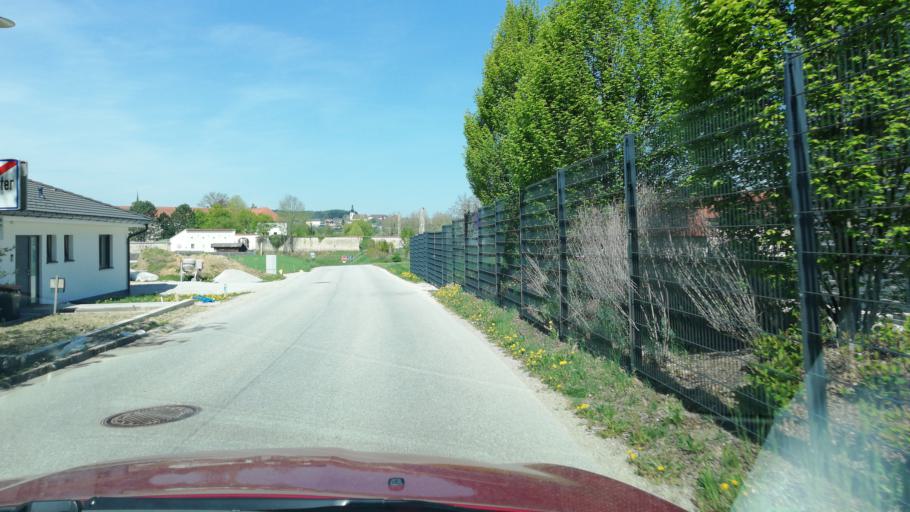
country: AT
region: Upper Austria
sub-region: Politischer Bezirk Kirchdorf an der Krems
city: Kremsmunster
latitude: 48.0528
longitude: 14.1492
